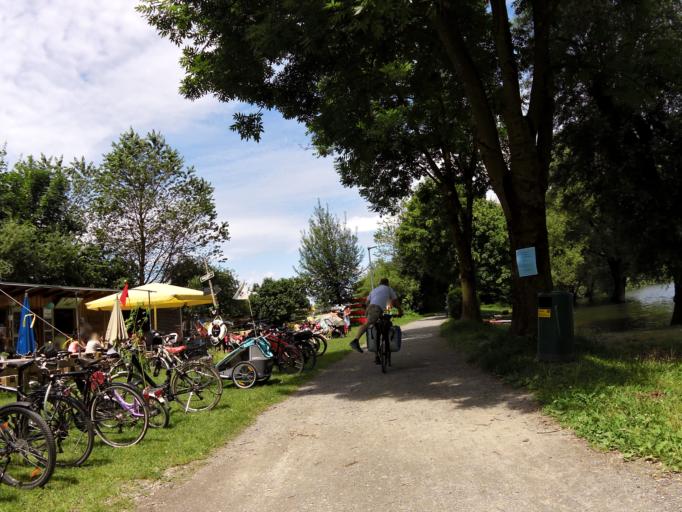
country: AT
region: Vorarlberg
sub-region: Politischer Bezirk Bregenz
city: Hard
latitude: 47.4926
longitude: 9.6791
